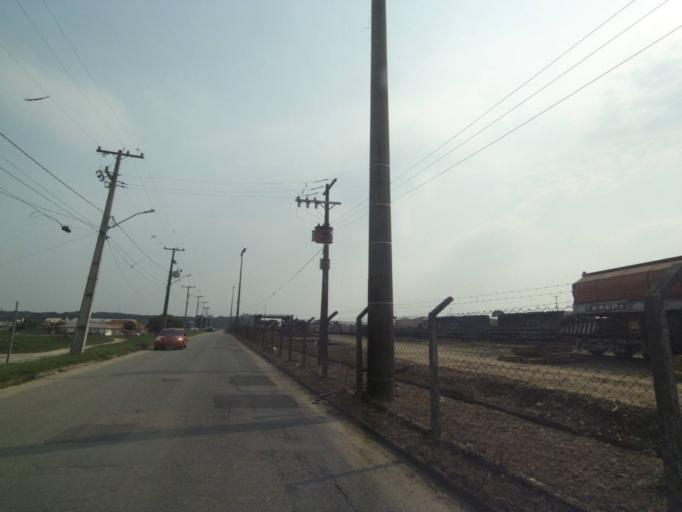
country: BR
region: Parana
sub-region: Sao Jose Dos Pinhais
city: Sao Jose dos Pinhais
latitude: -25.5347
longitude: -49.2321
